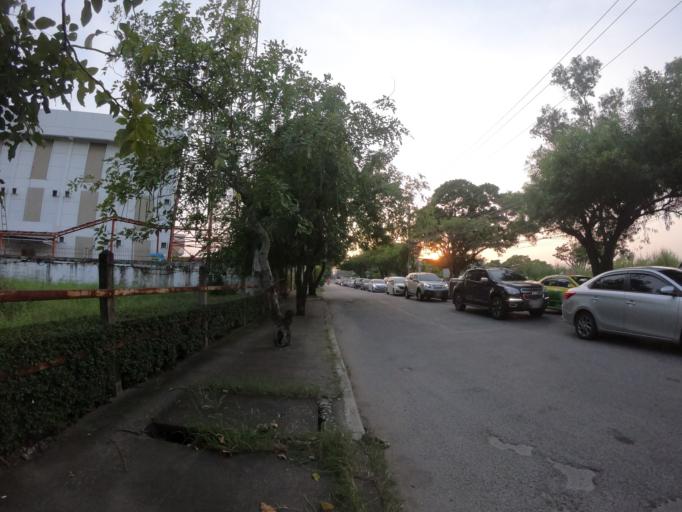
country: TH
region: Bangkok
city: Lat Phrao
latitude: 13.8315
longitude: 100.6104
